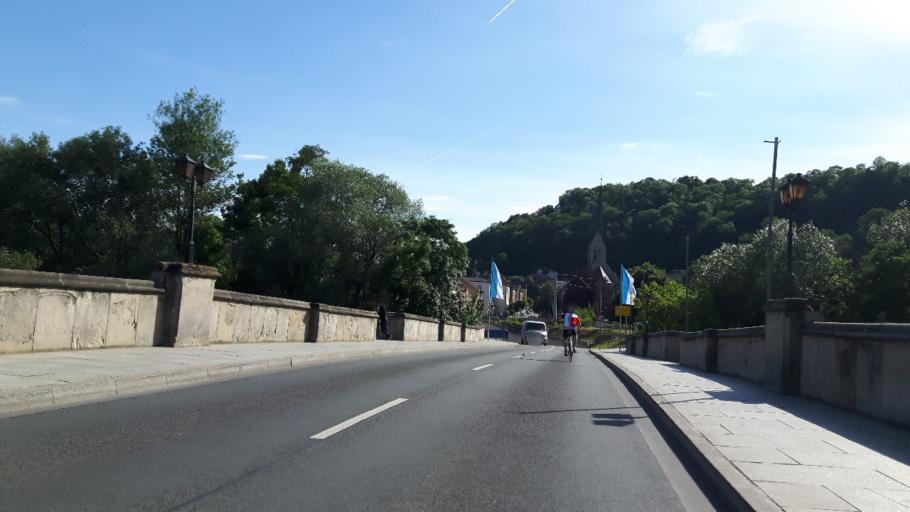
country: DE
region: Saxony-Anhalt
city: Bad Kosen
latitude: 51.1362
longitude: 11.7198
